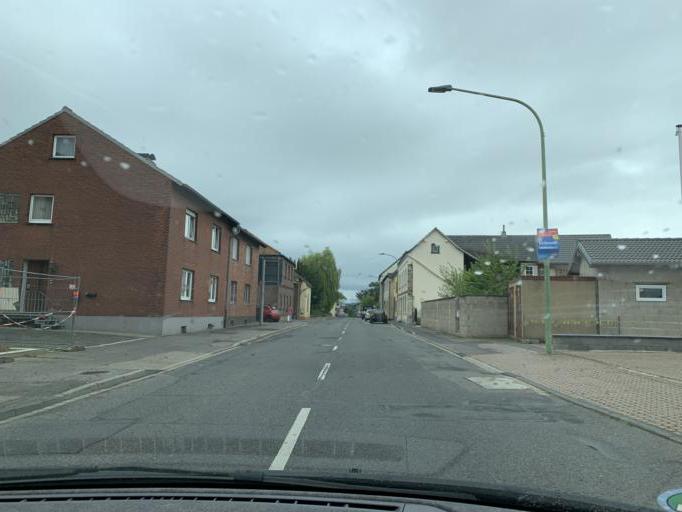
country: DE
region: North Rhine-Westphalia
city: Zulpich
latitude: 50.6874
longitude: 6.6453
